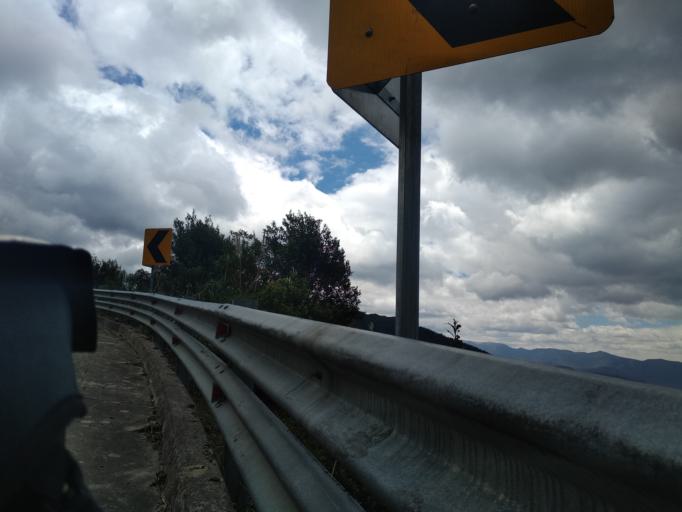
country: EC
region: Zamora-Chinchipe
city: Zamora
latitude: -4.4289
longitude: -79.1496
